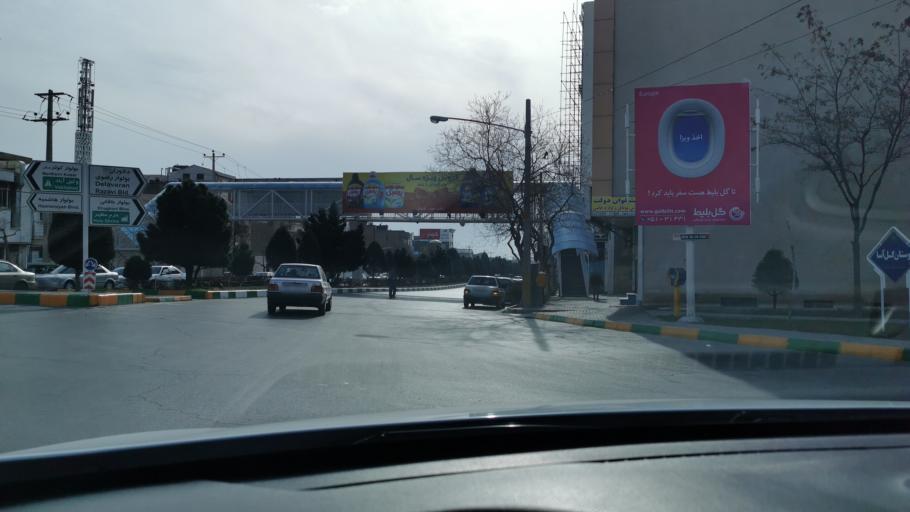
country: IR
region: Razavi Khorasan
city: Mashhad
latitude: 36.3046
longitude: 59.5127
